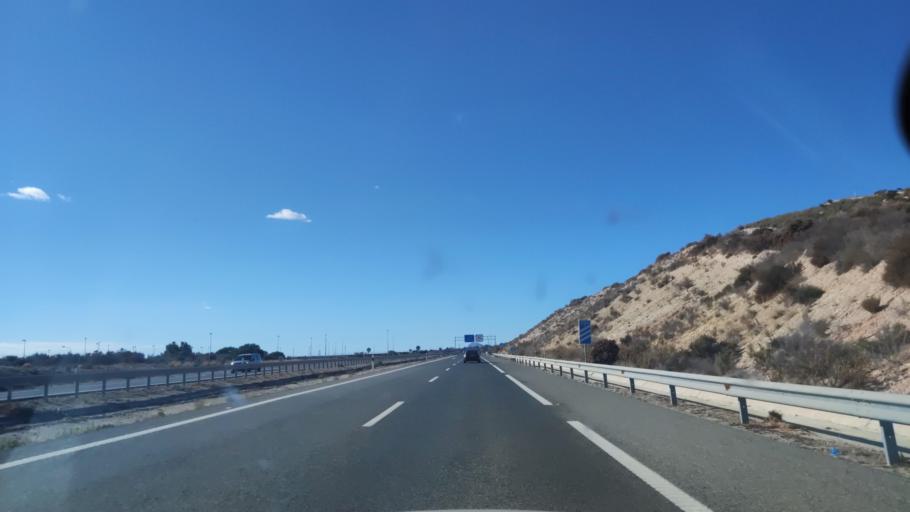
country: ES
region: Valencia
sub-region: Provincia de Alicante
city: el Campello
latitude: 38.4435
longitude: -0.3961
